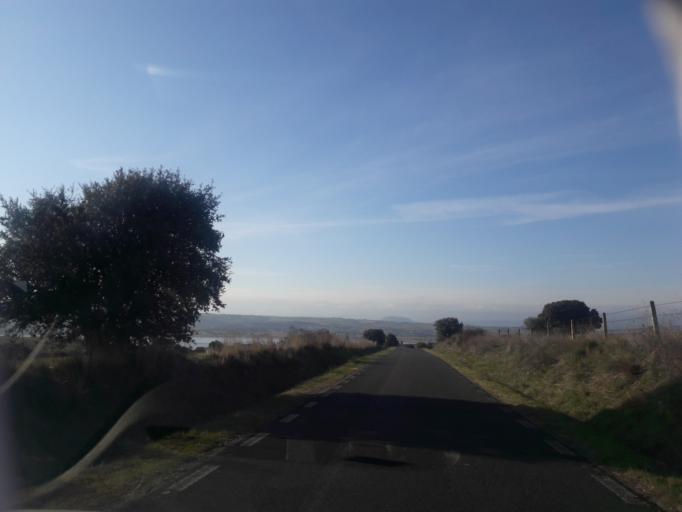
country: ES
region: Castille and Leon
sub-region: Provincia de Salamanca
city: Salvatierra de Tormes
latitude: 40.6010
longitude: -5.5998
